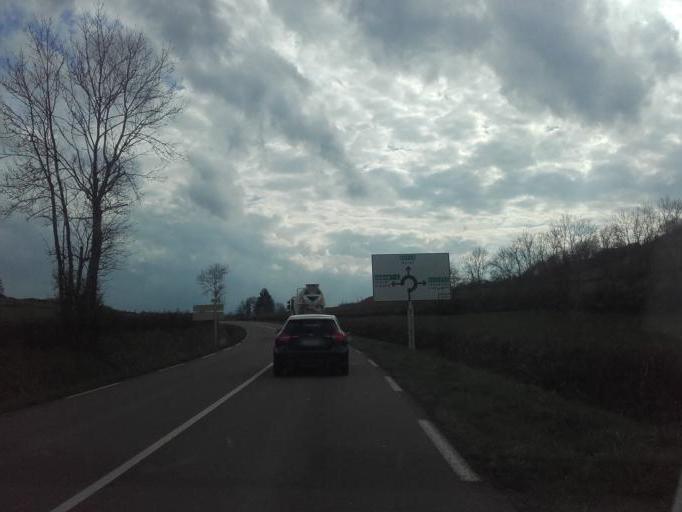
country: FR
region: Bourgogne
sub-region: Departement de la Cote-d'Or
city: Nolay
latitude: 46.9504
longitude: 4.6724
